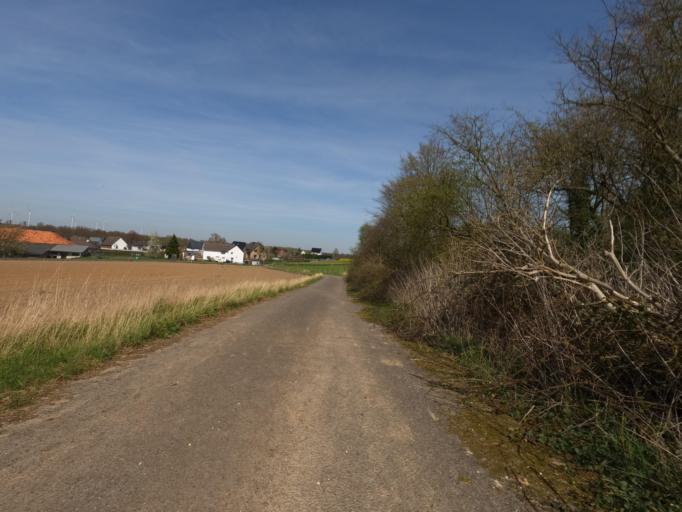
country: DE
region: North Rhine-Westphalia
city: Geilenkirchen
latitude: 50.9866
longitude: 6.1696
